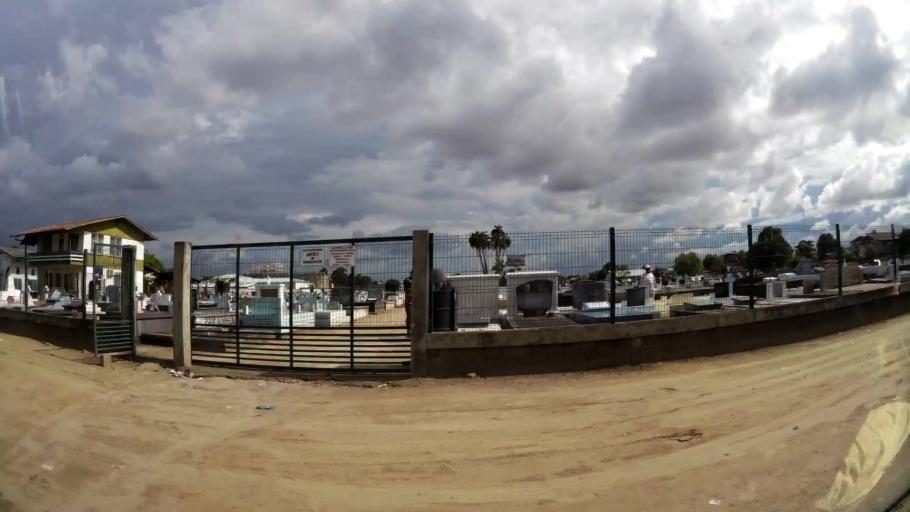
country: SR
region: Paramaribo
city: Paramaribo
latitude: 5.8402
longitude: -55.1542
